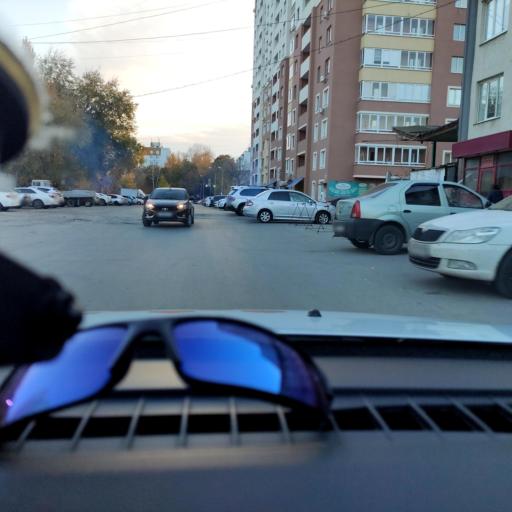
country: RU
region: Samara
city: Samara
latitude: 53.2243
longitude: 50.2004
